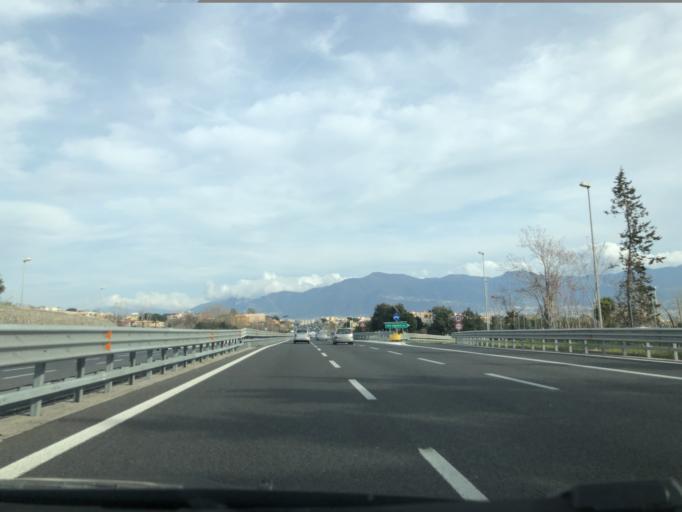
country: IT
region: Campania
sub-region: Provincia di Napoli
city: Trecase
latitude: 40.7673
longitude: 14.4274
